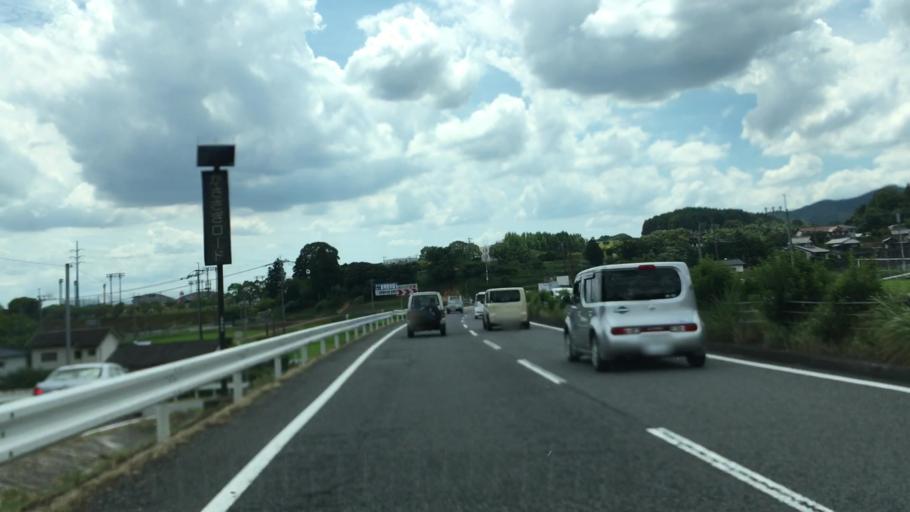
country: JP
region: Fukuoka
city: Chikushino-shi
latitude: 33.4346
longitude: 130.5245
